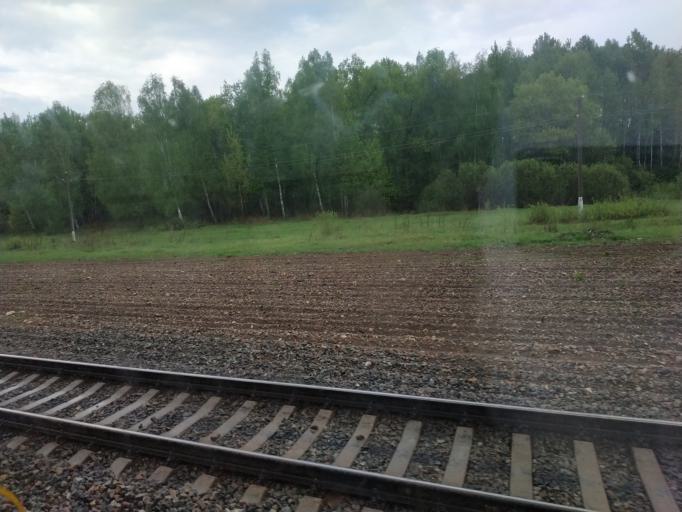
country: RU
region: Kaluga
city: Baryatino
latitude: 54.3529
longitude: 34.3234
